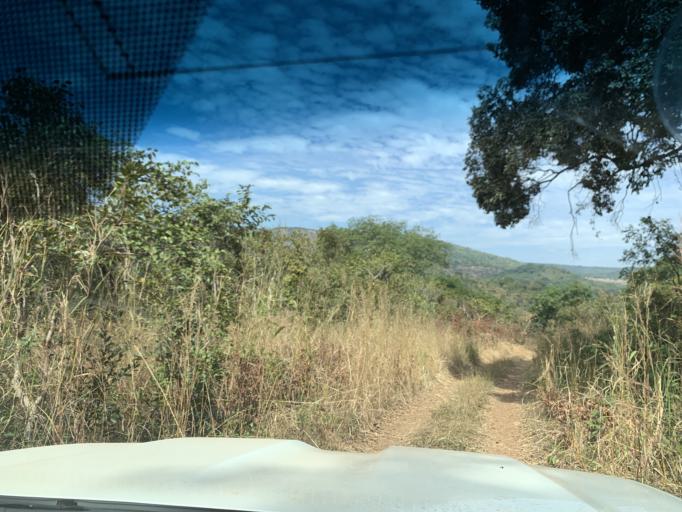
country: GN
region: Mamou
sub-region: Pita
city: Pita
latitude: 10.9940
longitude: -12.4891
